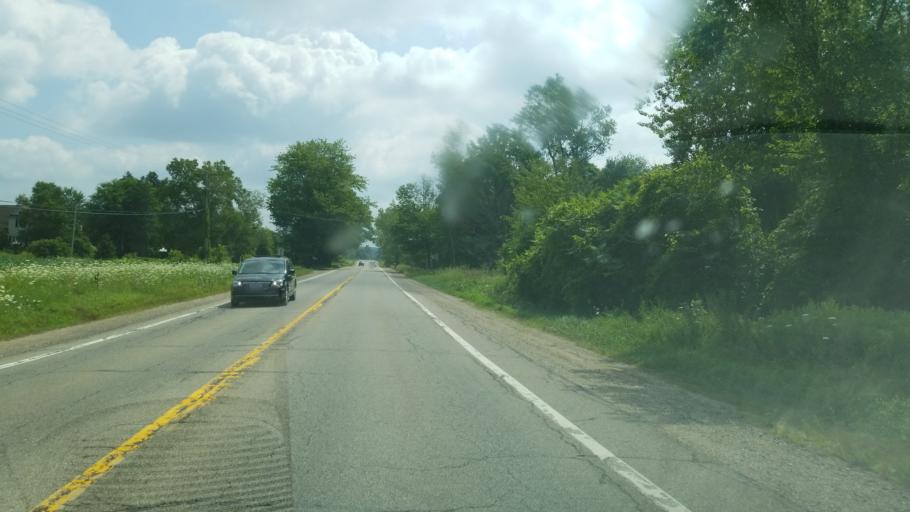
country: US
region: Michigan
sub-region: Kent County
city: Kent City
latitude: 43.2197
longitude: -85.6990
